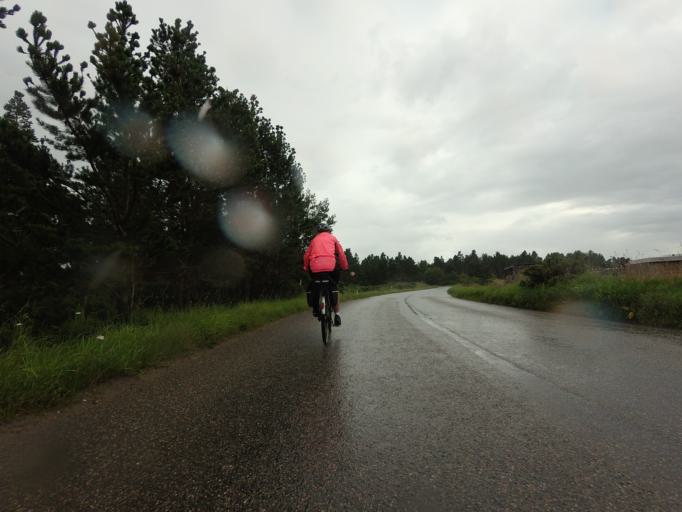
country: GB
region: Scotland
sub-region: Moray
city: Fochabers
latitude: 57.6569
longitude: -3.0571
